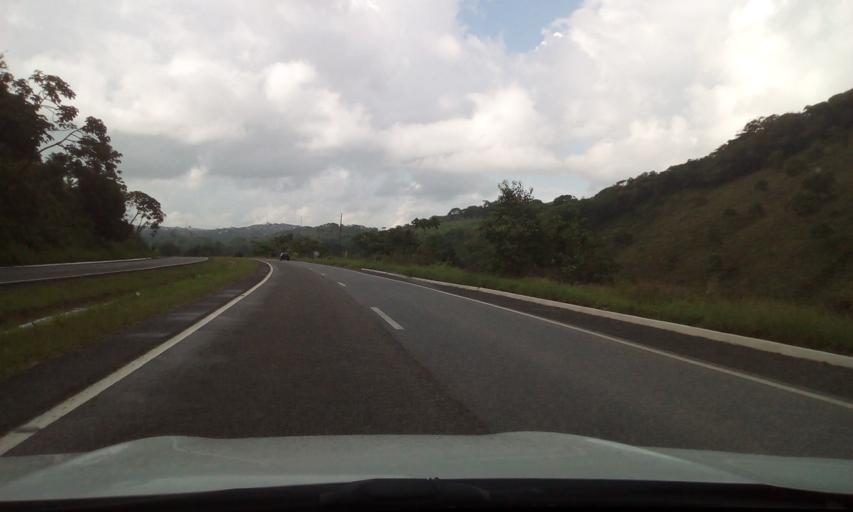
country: BR
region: Pernambuco
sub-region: Cabo De Santo Agostinho
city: Cabo
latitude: -8.2686
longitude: -35.0534
